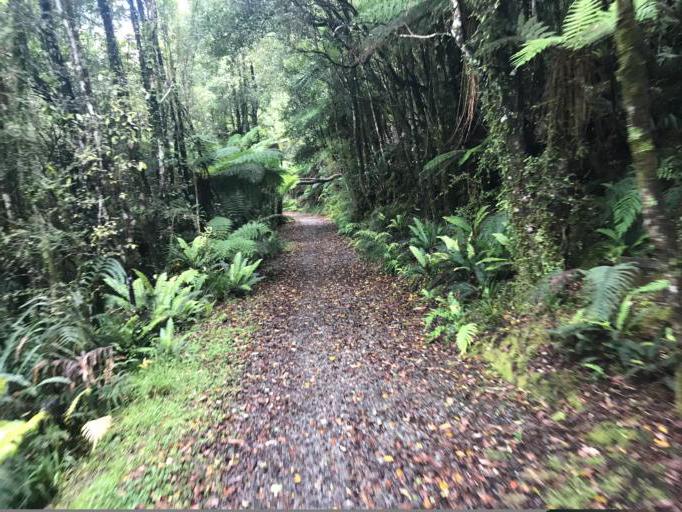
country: NZ
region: West Coast
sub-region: Westland District
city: Hokitika
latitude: -42.7650
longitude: 171.2484
